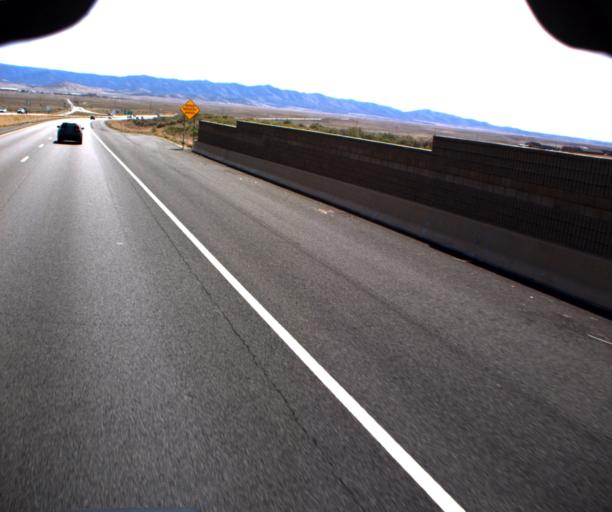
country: US
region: Arizona
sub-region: Yavapai County
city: Prescott Valley
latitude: 34.6391
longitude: -112.3229
